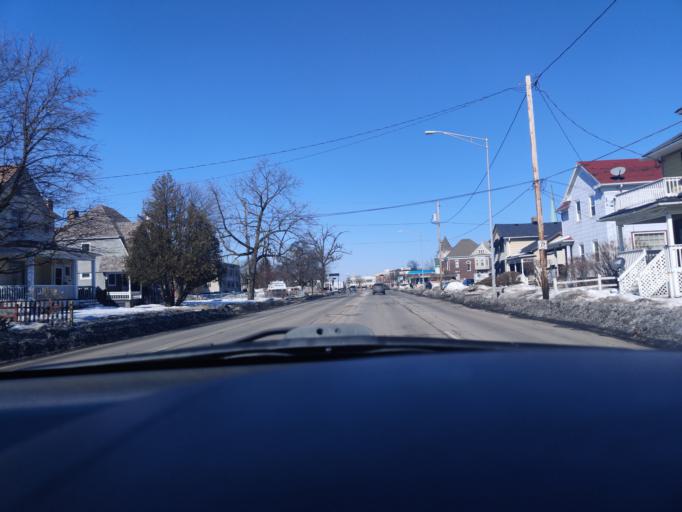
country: US
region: Wisconsin
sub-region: Kenosha County
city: Kenosha
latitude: 42.5789
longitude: -87.8215
